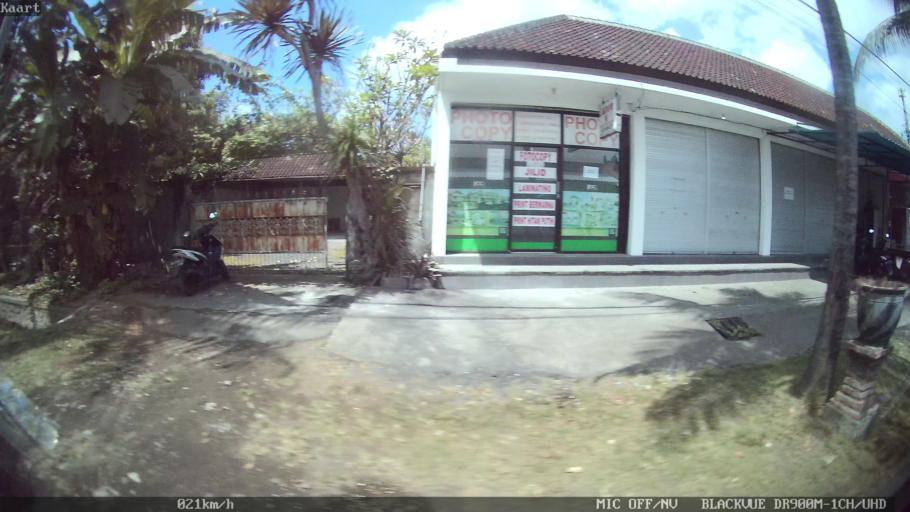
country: ID
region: Bali
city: Banjar Pasekan
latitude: -8.5920
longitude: 115.2847
